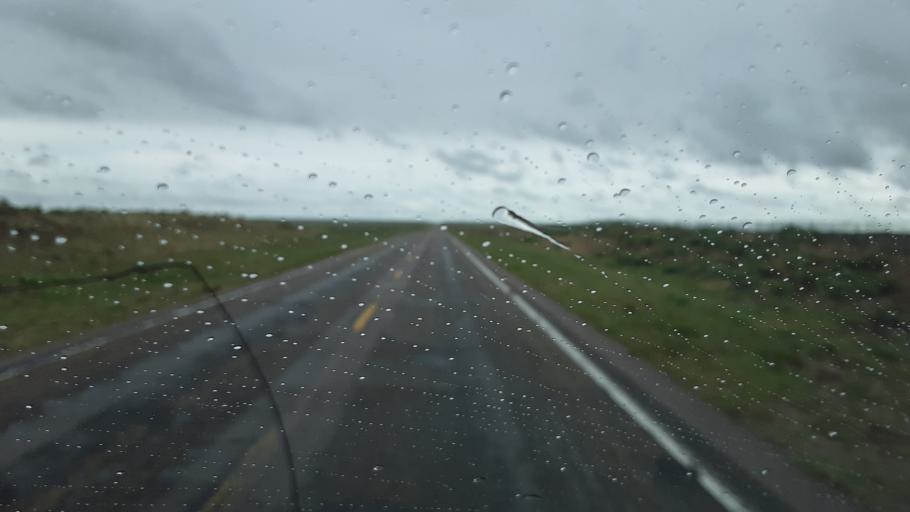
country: US
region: Colorado
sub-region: Lincoln County
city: Hugo
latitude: 38.8496
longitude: -103.2898
